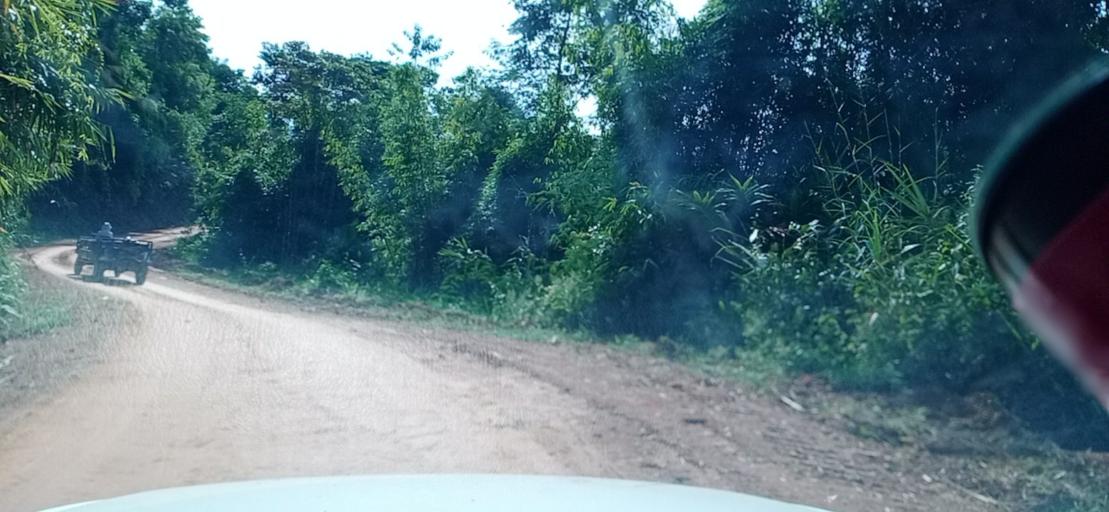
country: TH
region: Changwat Bueng Kan
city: Pak Khat
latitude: 18.6367
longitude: 103.2488
